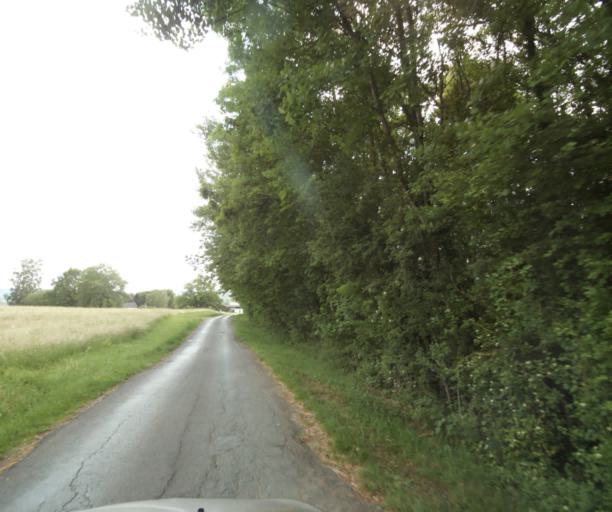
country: FR
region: Champagne-Ardenne
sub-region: Departement des Ardennes
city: Montcy-Notre-Dame
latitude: 49.7639
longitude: 4.7334
